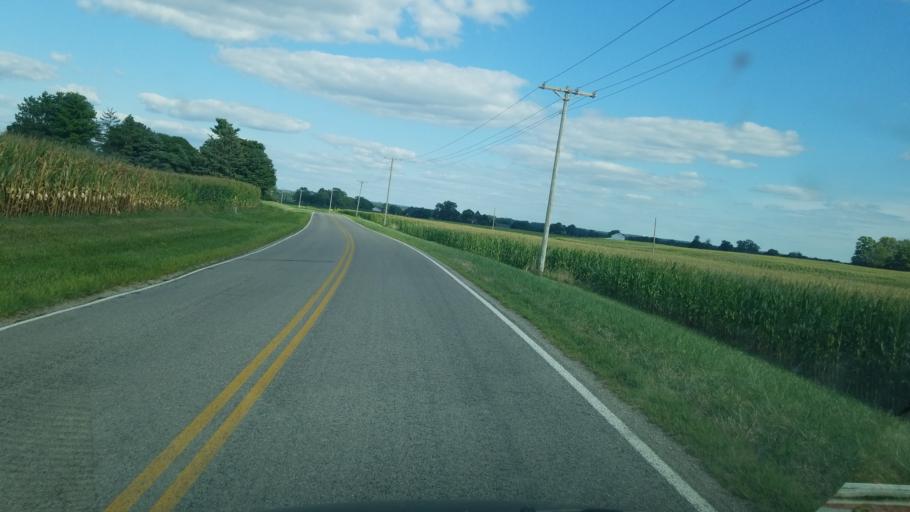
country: US
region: Ohio
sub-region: Champaign County
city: Urbana
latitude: 40.1319
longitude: -83.8479
